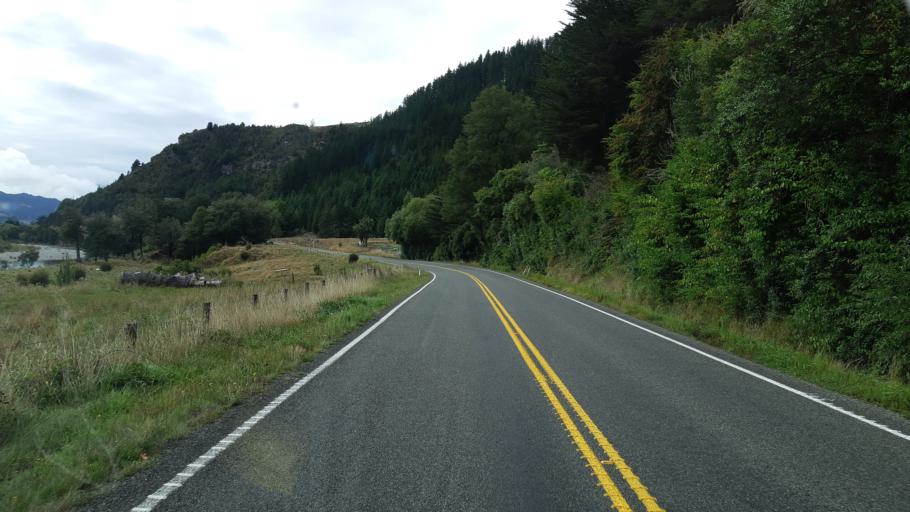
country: NZ
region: West Coast
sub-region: Buller District
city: Westport
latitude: -41.7808
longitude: 172.2599
